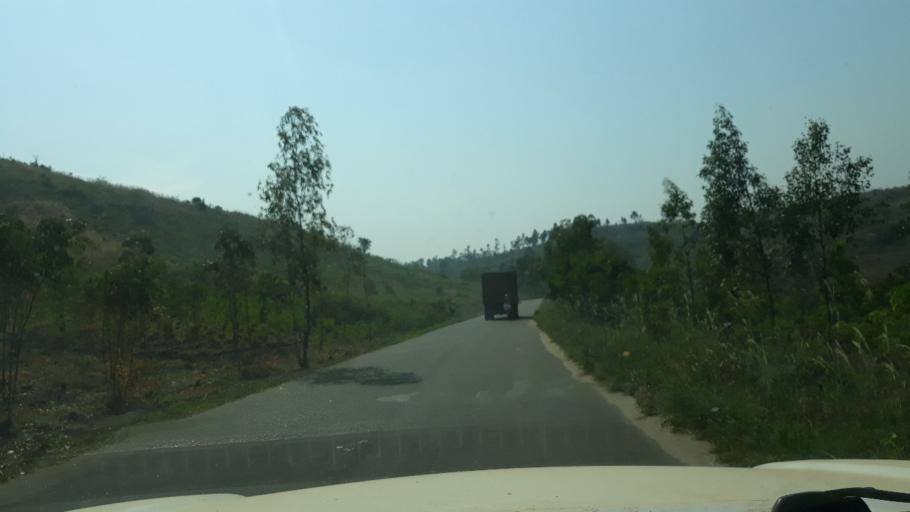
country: CD
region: South Kivu
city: Uvira
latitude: -3.2032
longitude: 29.1604
